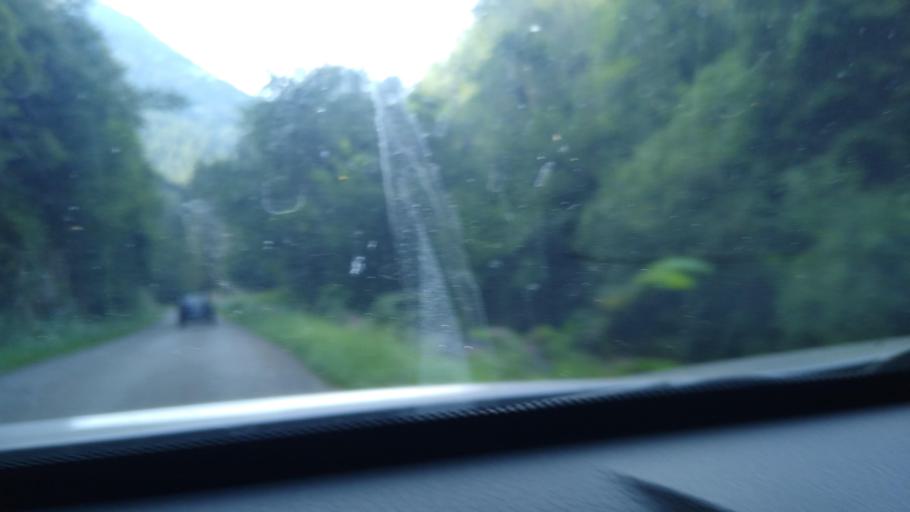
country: FR
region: Midi-Pyrenees
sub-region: Departement de l'Ariege
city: Saint-Girons
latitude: 42.8137
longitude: 1.1958
